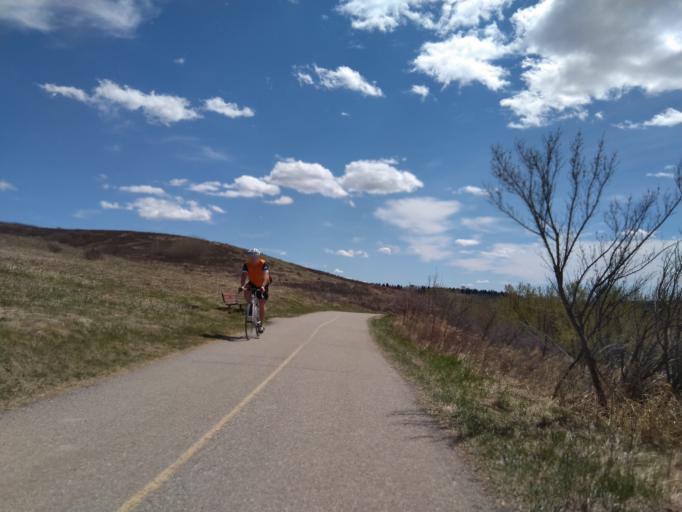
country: CA
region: Alberta
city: Calgary
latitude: 51.0942
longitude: -114.1839
